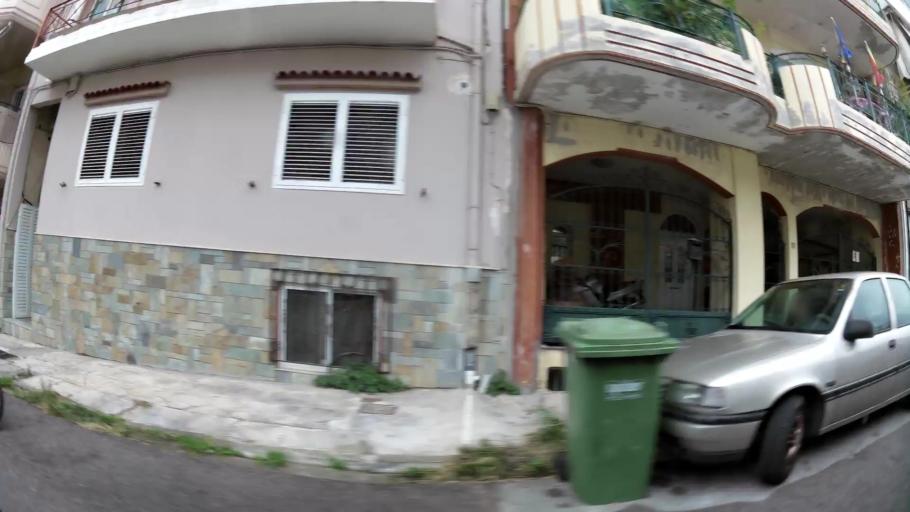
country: GR
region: Attica
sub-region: Nomos Piraios
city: Korydallos
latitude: 37.9874
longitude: 23.6467
